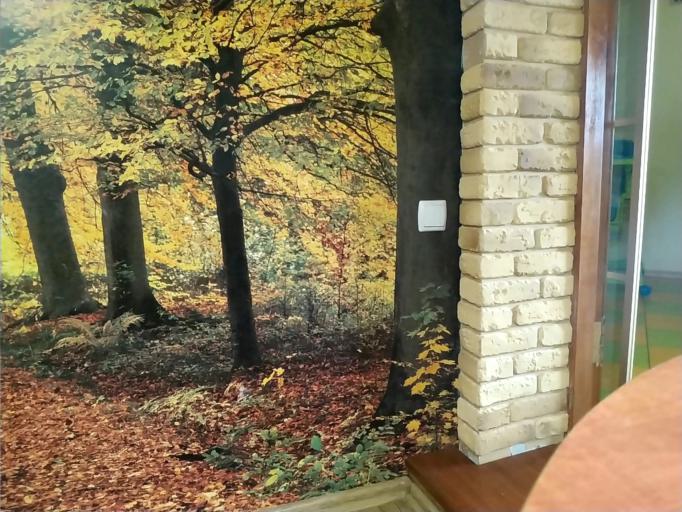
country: RU
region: Smolensk
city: Dorogobuzh
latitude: 54.8632
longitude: 33.3140
